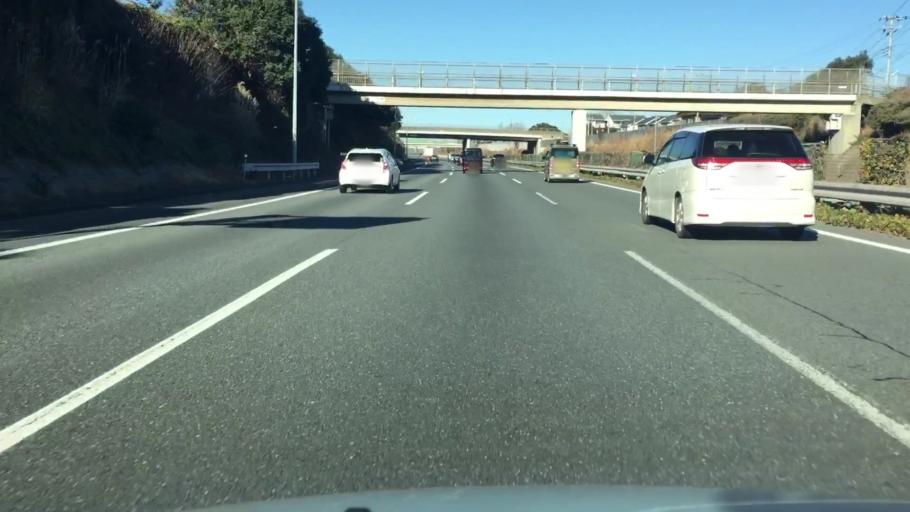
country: JP
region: Saitama
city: Sakado
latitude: 36.0393
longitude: 139.3730
